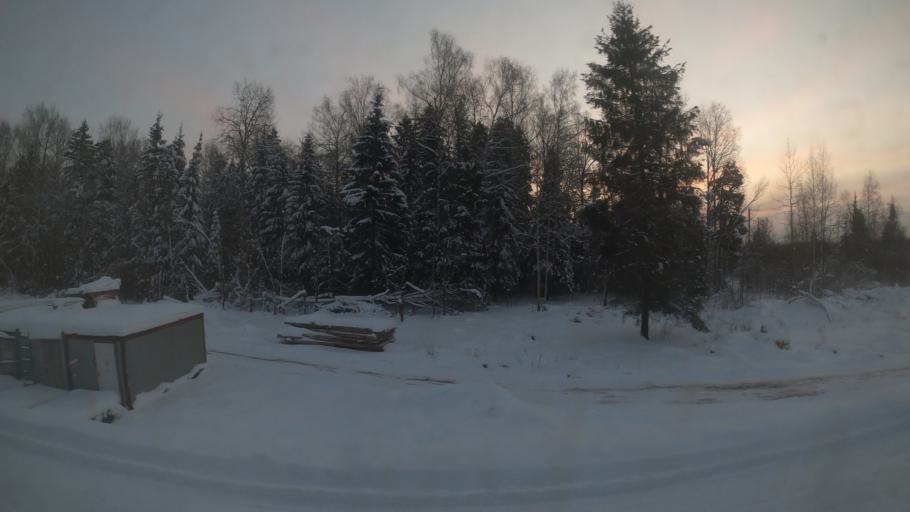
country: RU
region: Moskovskaya
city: Lugovaya
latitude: 56.0347
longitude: 37.4887
